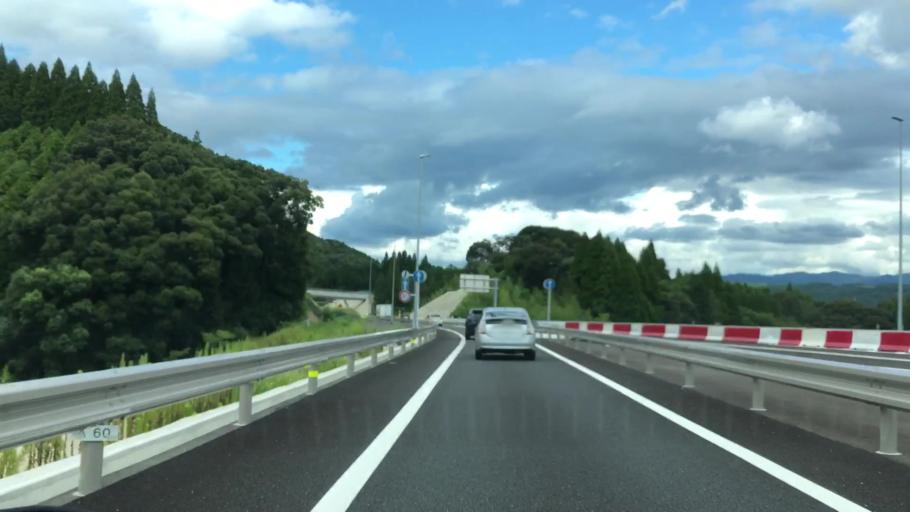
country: JP
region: Saga Prefecture
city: Imaricho-ko
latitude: 33.2980
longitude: 129.9132
